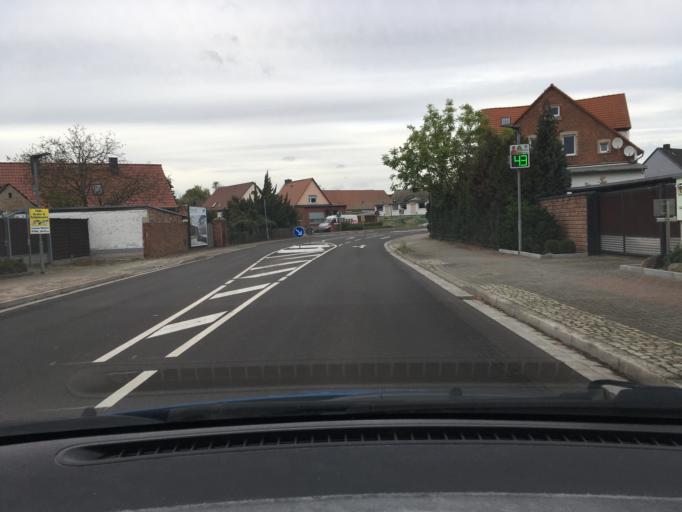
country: DE
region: Saxony-Anhalt
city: Wahlitz
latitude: 52.1042
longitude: 11.7808
